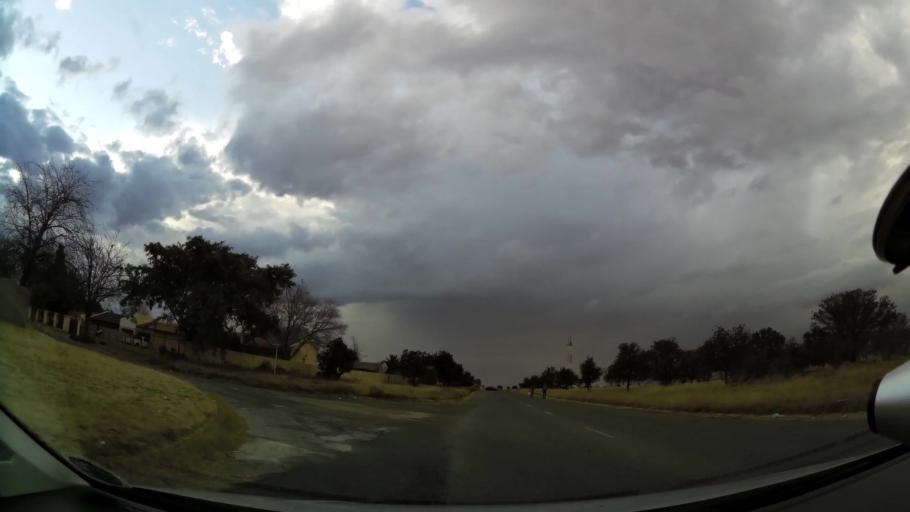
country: ZA
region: Orange Free State
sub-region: Lejweleputswa District Municipality
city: Welkom
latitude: -27.9493
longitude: 26.7348
